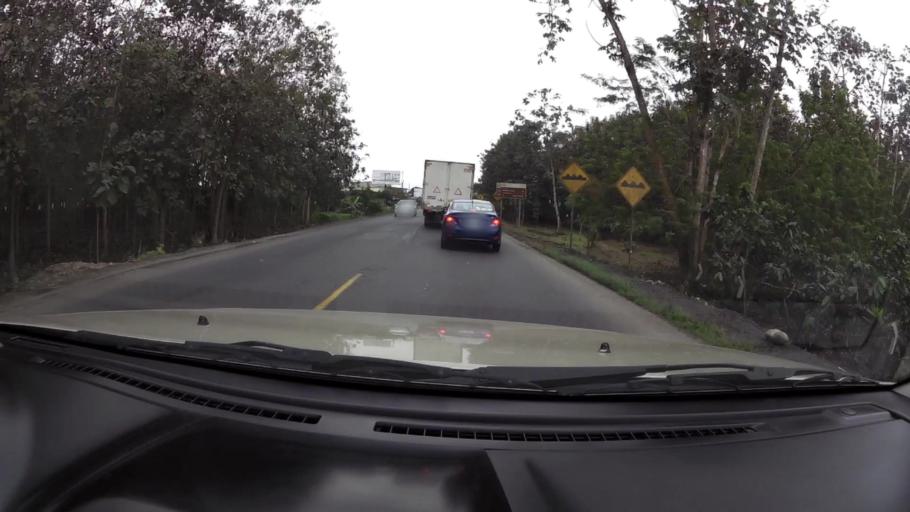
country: EC
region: Guayas
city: Naranjal
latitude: -2.7979
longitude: -79.7074
